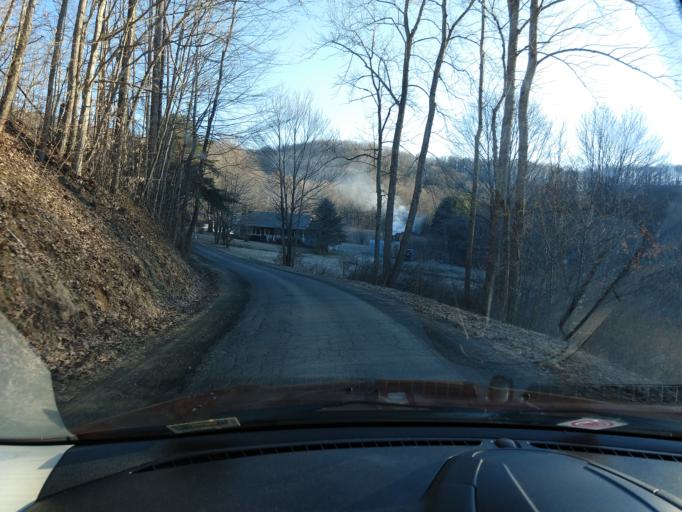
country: US
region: West Virginia
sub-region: Greenbrier County
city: Rainelle
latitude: 37.9032
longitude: -80.7354
